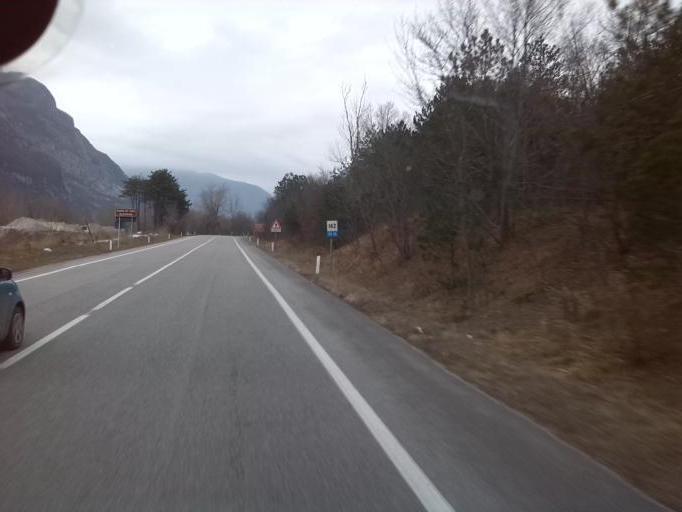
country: IT
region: Friuli Venezia Giulia
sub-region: Provincia di Udine
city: Venzone
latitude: 46.3132
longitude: 13.1287
